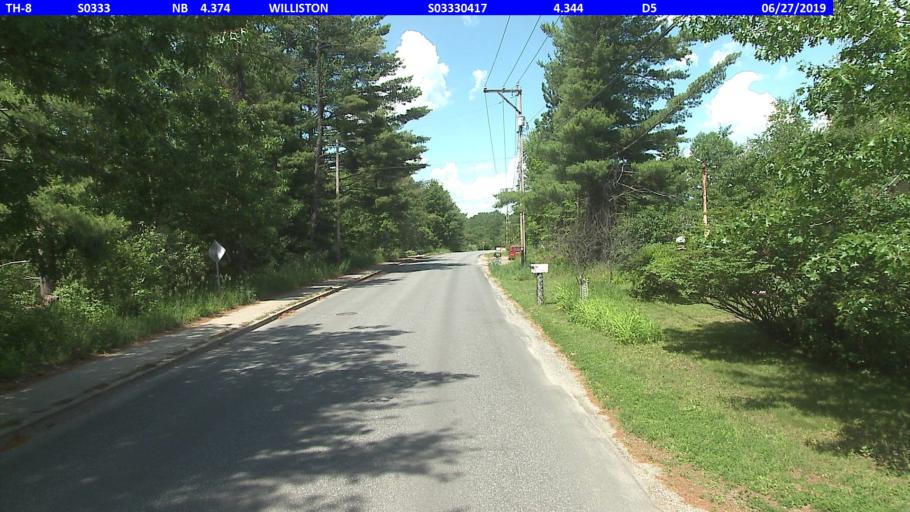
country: US
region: Vermont
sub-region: Chittenden County
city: Essex Junction
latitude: 44.4616
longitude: -73.1196
